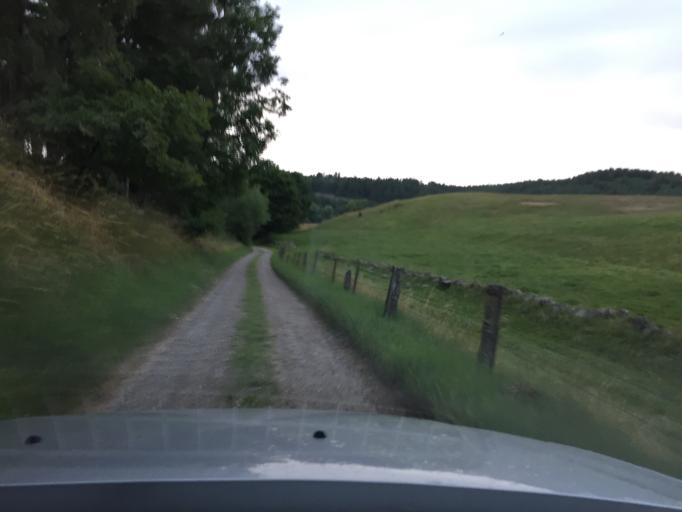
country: SE
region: Skane
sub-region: Kristianstads Kommun
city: Degeberga
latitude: 55.7241
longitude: 14.1278
